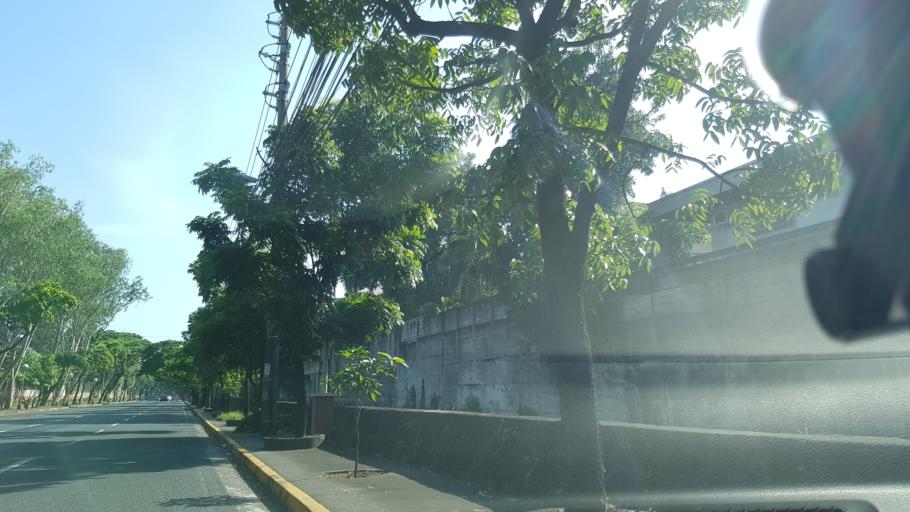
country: PH
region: Metro Manila
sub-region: Pasig
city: Pasig City
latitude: 14.5868
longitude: 121.0711
